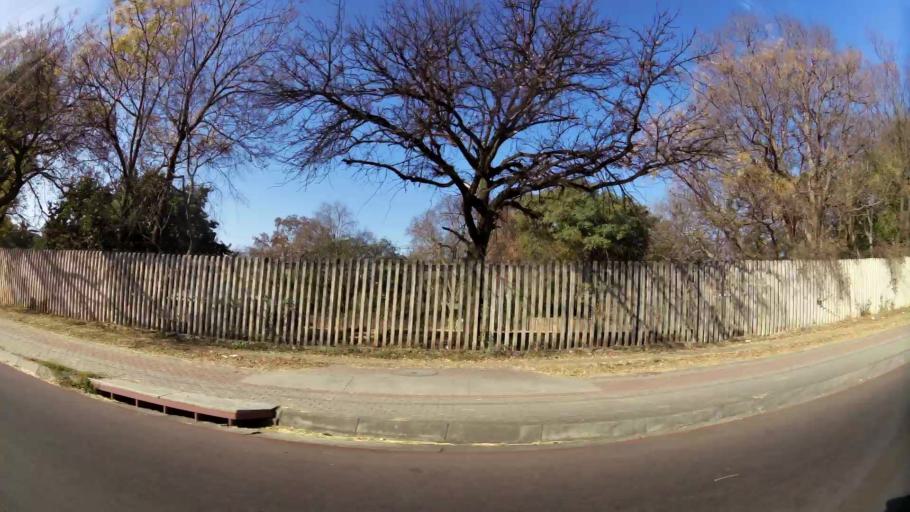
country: ZA
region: Gauteng
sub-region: City of Tshwane Metropolitan Municipality
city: Pretoria
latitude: -25.7361
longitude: 28.1872
